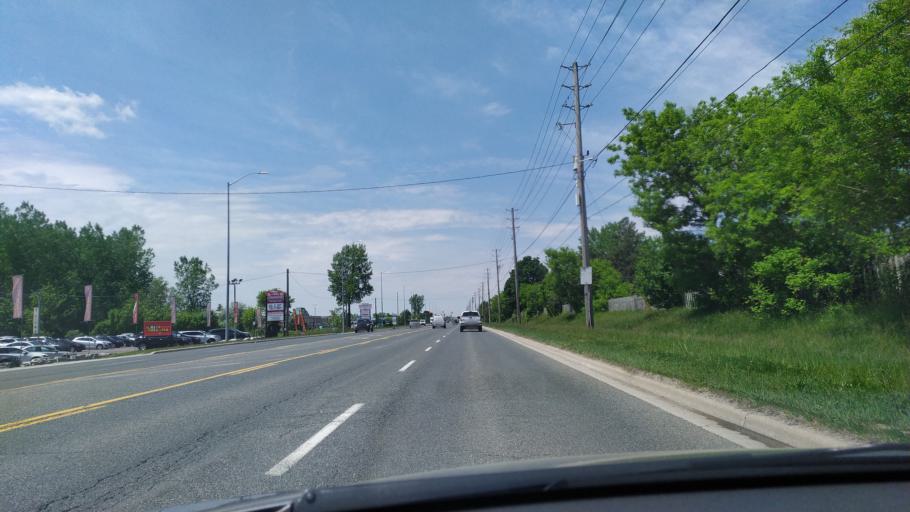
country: CA
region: Ontario
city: London
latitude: 42.9243
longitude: -81.2362
